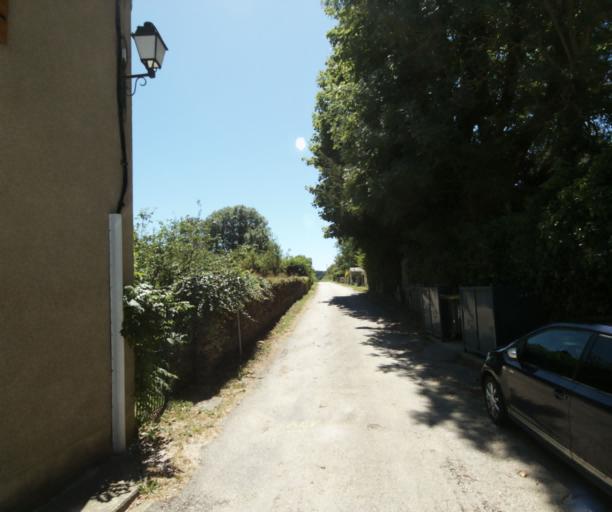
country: FR
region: Midi-Pyrenees
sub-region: Departement du Tarn
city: Dourgne
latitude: 43.4292
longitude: 2.1664
